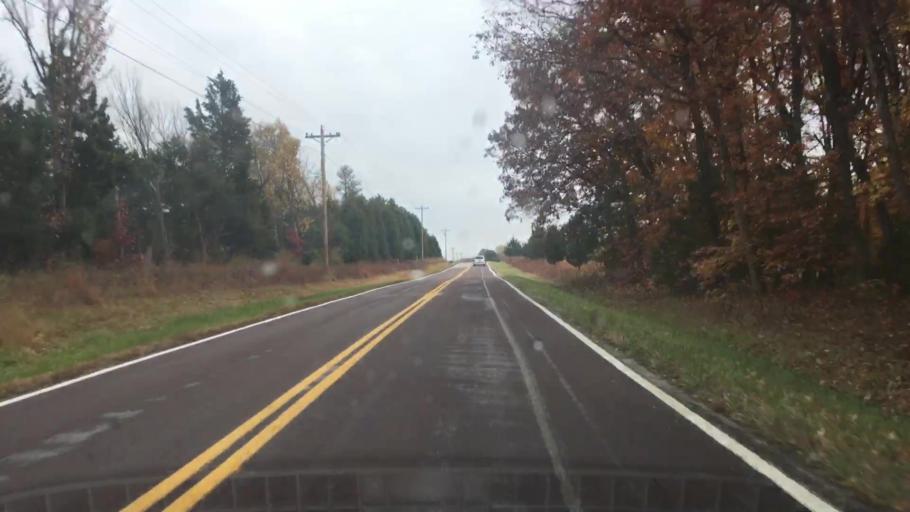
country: US
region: Missouri
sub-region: Callaway County
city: Fulton
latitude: 38.7827
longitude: -91.8256
